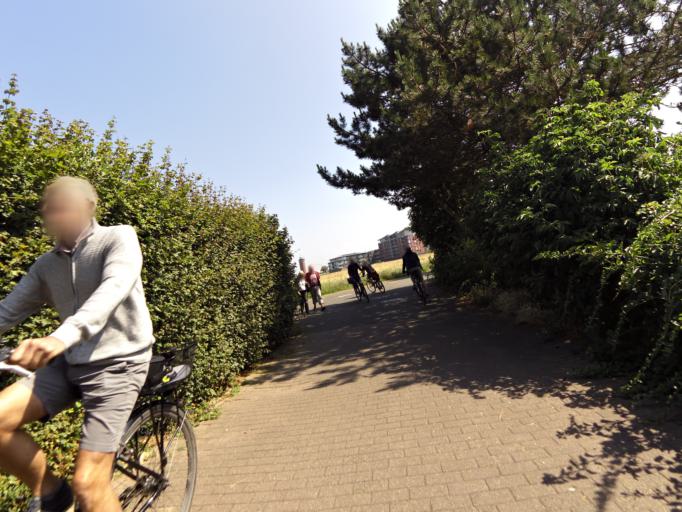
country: DE
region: Lower Saxony
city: Cuxhaven
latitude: 53.8742
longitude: 8.7041
